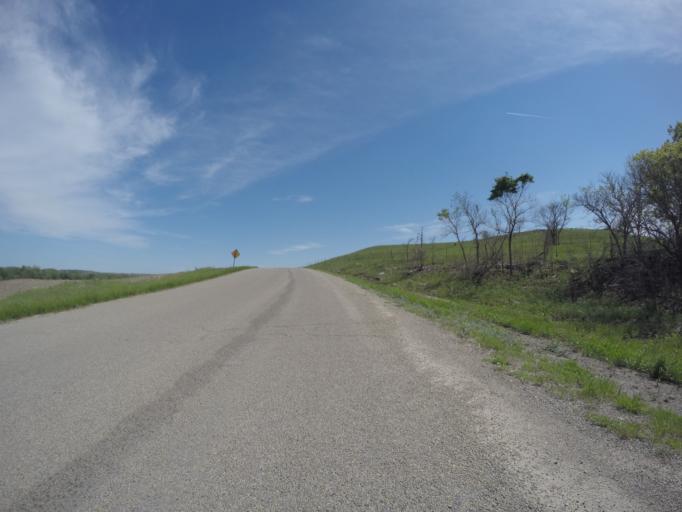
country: US
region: Kansas
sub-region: Riley County
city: Ogden
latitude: 39.0351
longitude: -96.6230
